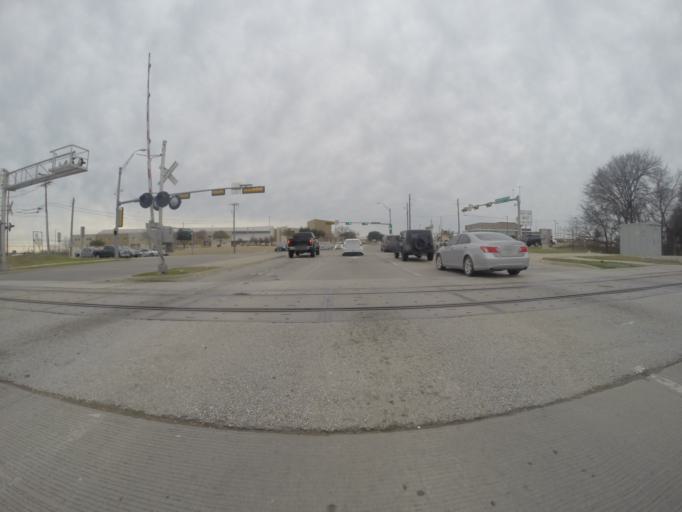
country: US
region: Texas
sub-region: Collin County
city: Saint Paul
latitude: 33.0328
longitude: -96.5687
